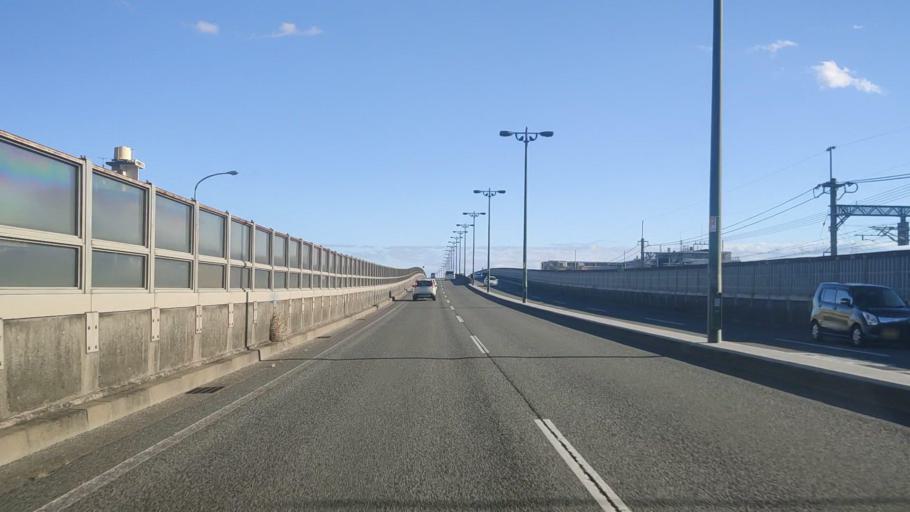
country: JP
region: Fukuoka
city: Dazaifu
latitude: 33.5168
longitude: 130.5004
